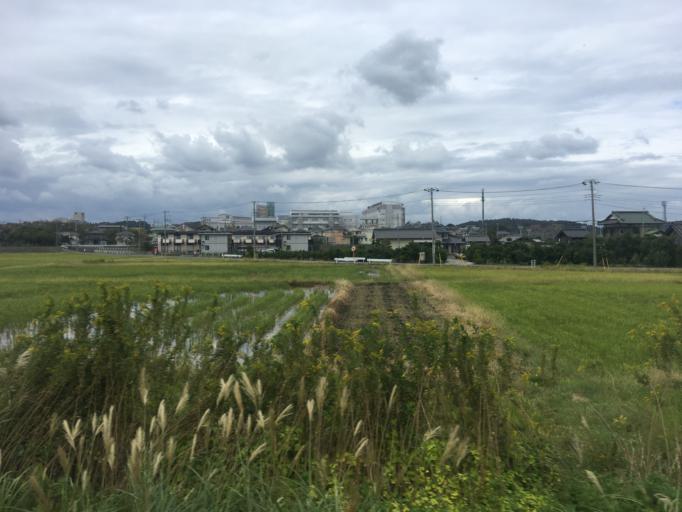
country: JP
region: Chiba
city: Naruto
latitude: 35.5809
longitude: 140.3974
